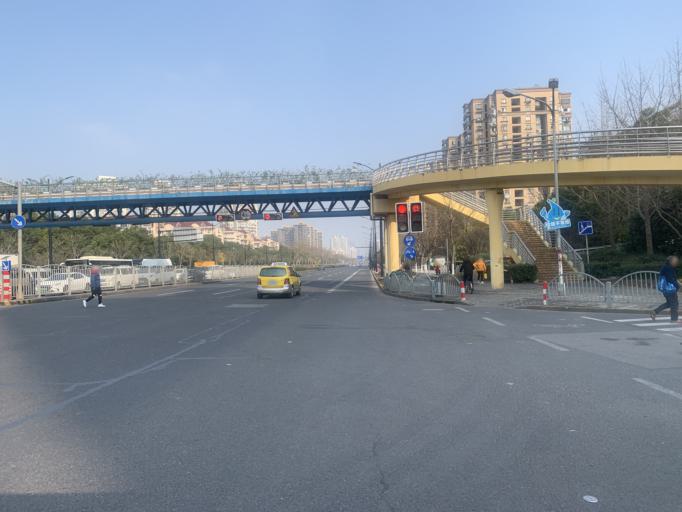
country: CN
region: Shanghai Shi
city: Huamu
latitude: 31.1819
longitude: 121.5164
